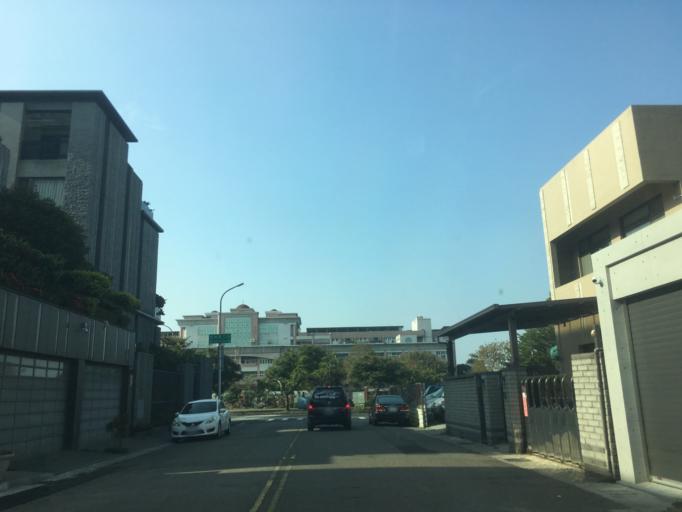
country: TW
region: Taiwan
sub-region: Taichung City
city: Taichung
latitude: 24.1958
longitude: 120.6768
